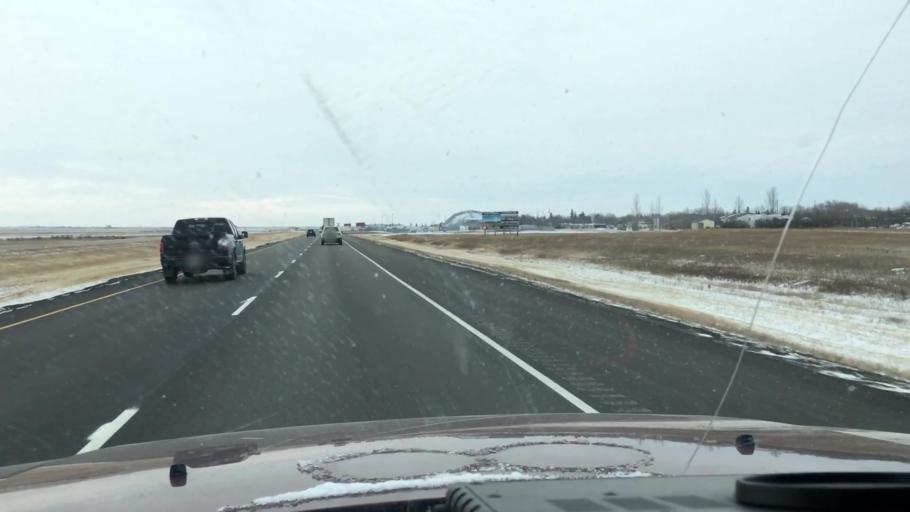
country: CA
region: Saskatchewan
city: Saskatoon
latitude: 51.8203
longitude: -106.4992
